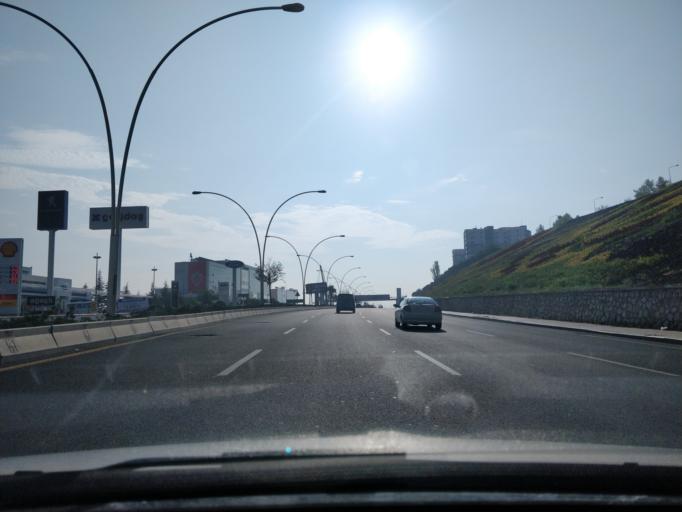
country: TR
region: Ankara
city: Batikent
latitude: 39.9050
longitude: 32.6977
